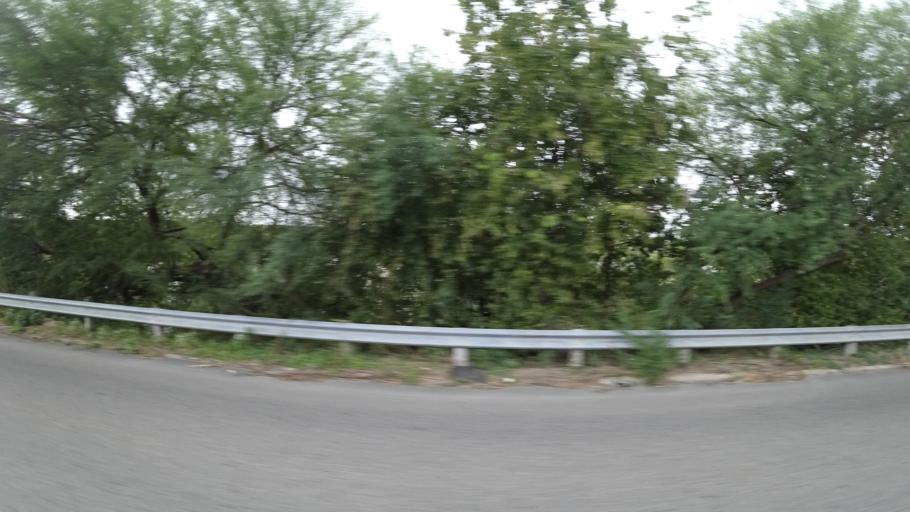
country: US
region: Texas
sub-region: Travis County
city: Austin
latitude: 30.2734
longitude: -97.7655
